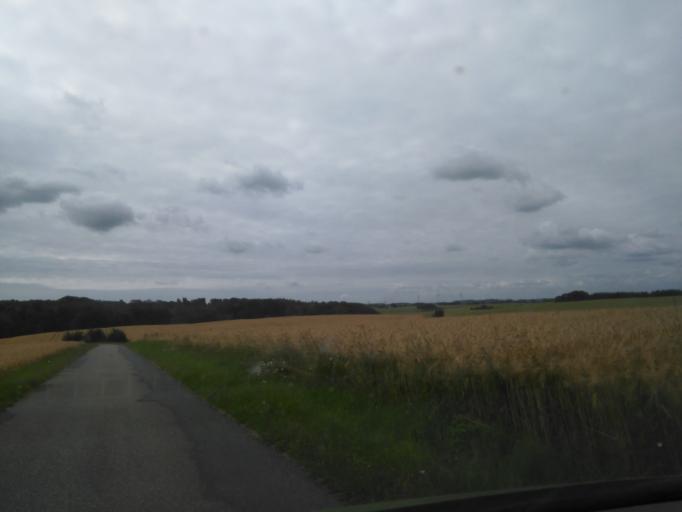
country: DK
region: Central Jutland
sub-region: Arhus Kommune
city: Solbjerg
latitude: 56.0030
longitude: 10.0550
